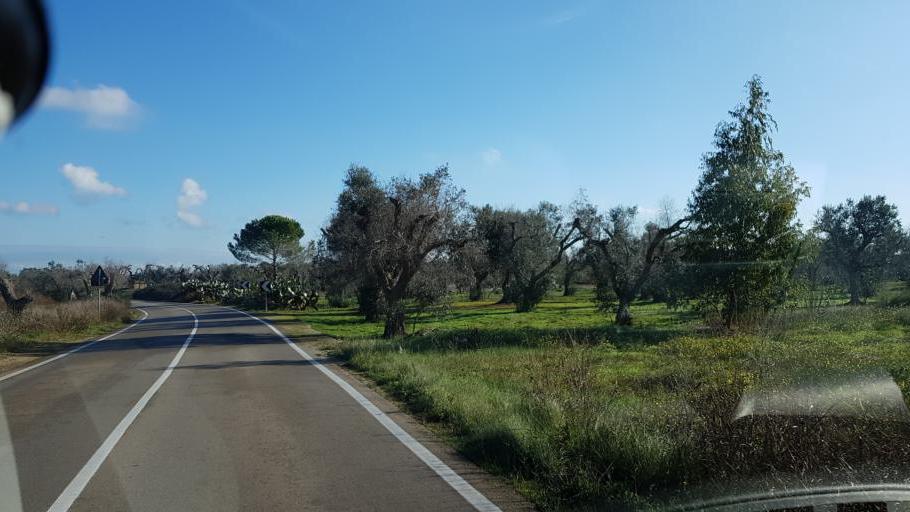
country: IT
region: Apulia
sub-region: Provincia di Lecce
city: Trepuzzi
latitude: 40.4404
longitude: 18.0852
